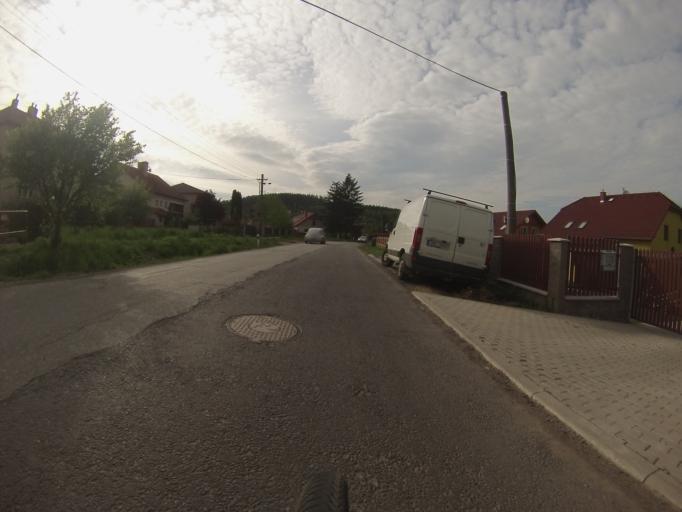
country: CZ
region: South Moravian
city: Cebin
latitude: 49.3115
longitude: 16.4551
